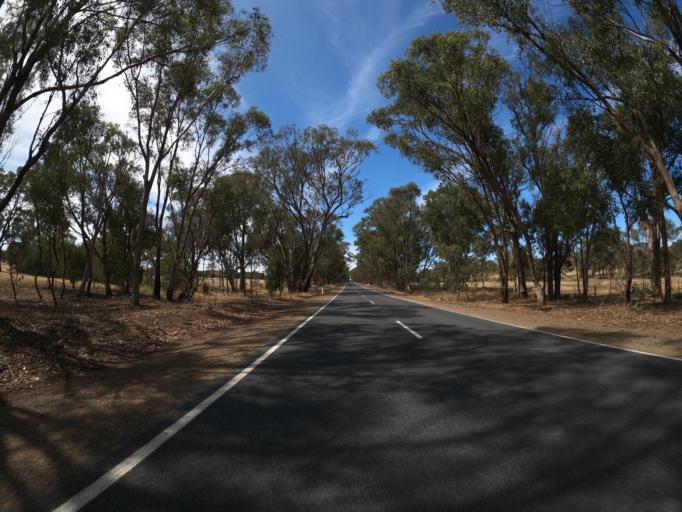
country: AU
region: Victoria
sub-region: Benalla
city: Benalla
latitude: -36.3654
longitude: 145.9698
